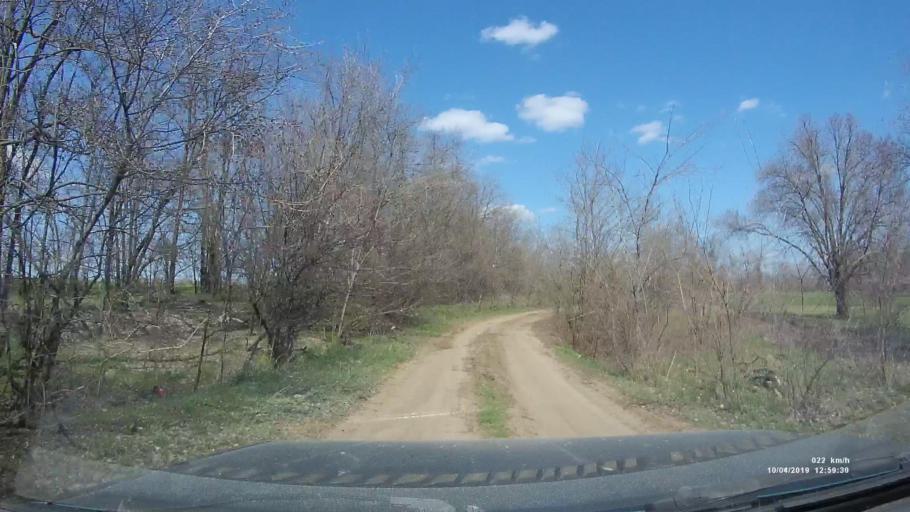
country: RU
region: Rostov
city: Masalovka
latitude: 48.3778
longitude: 40.2281
